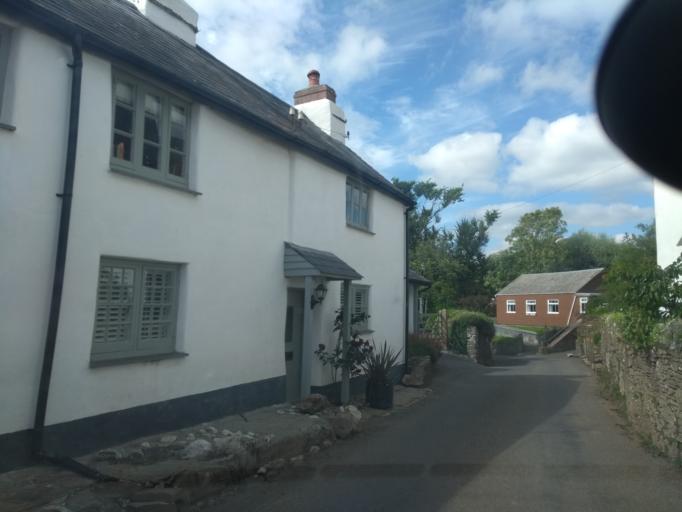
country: GB
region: England
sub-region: Devon
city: Modbury
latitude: 50.2973
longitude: -3.8931
